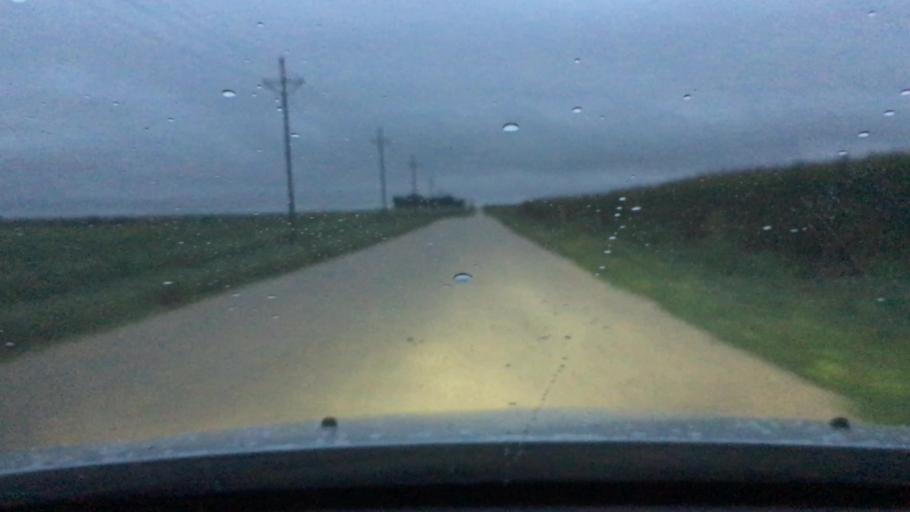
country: US
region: Illinois
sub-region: Ogle County
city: Rochelle
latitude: 41.8986
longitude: -88.9923
